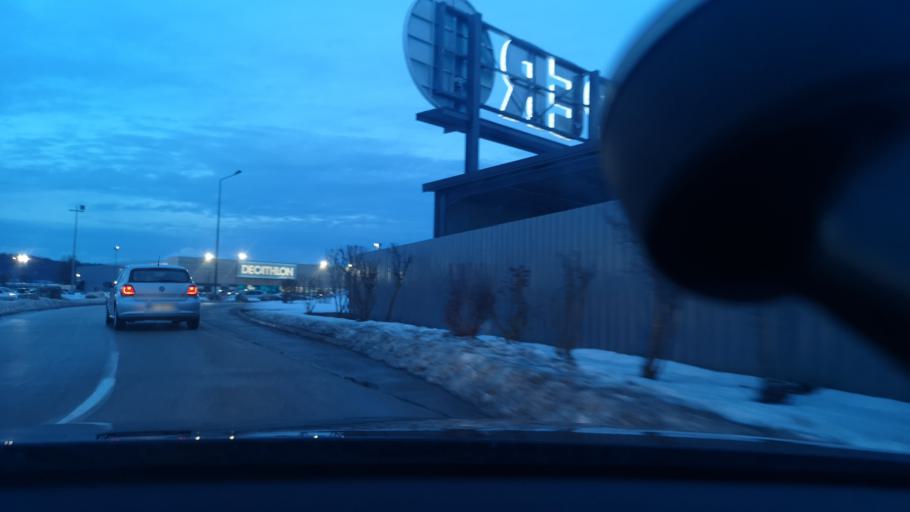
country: FR
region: Franche-Comte
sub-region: Departement du Doubs
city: Doubs
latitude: 46.9230
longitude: 6.3399
